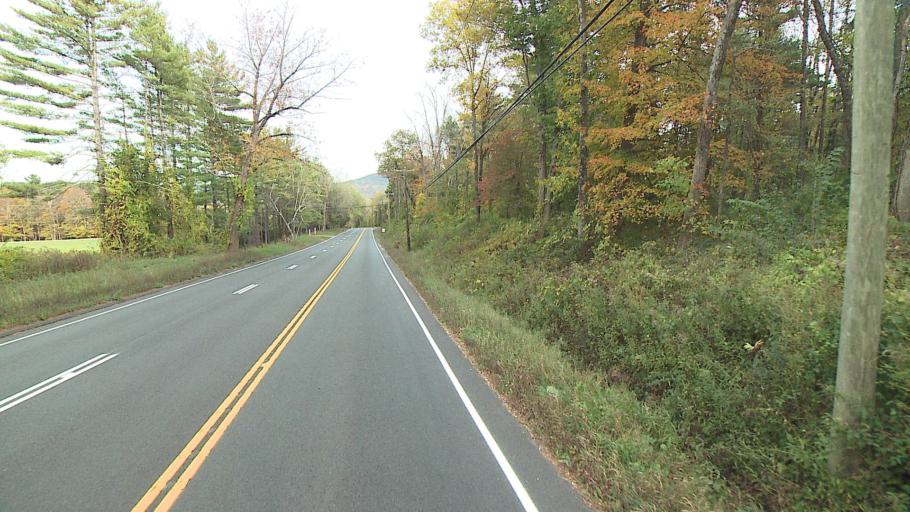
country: US
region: Connecticut
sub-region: Litchfield County
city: Canaan
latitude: 42.0030
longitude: -73.3790
